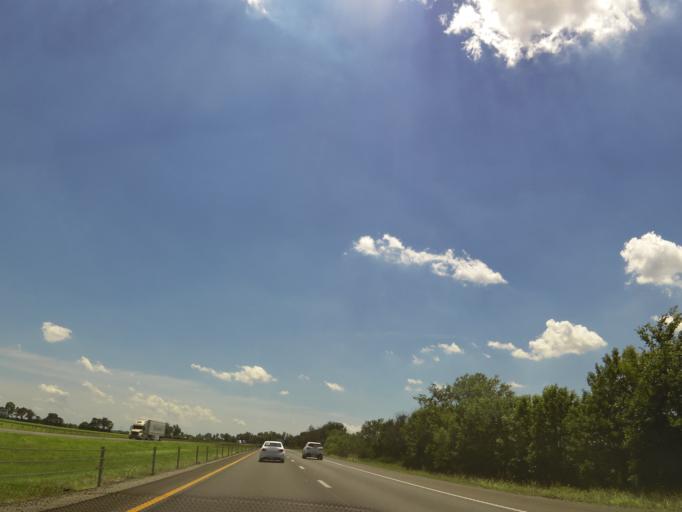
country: US
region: Missouri
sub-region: New Madrid County
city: Portageville
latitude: 36.3917
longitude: -89.6994
